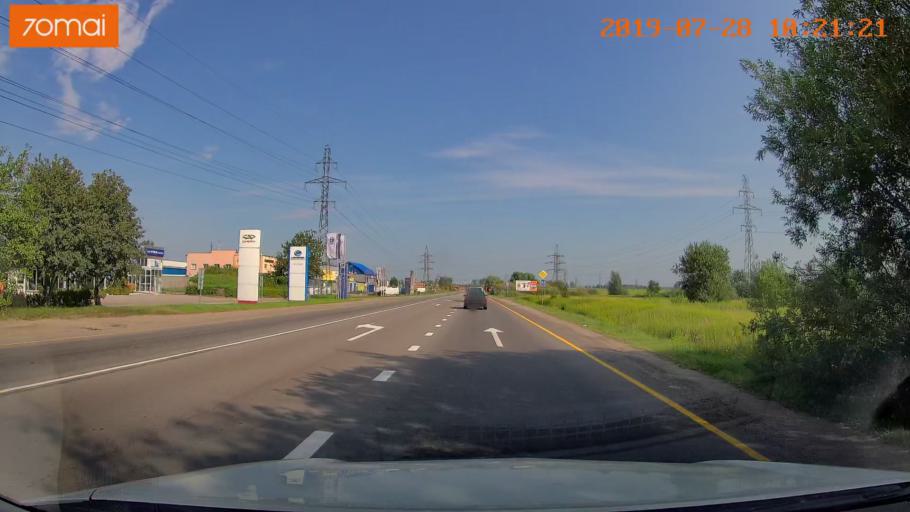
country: RU
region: Kaliningrad
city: Maloye Isakovo
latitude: 54.7566
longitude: 20.5644
